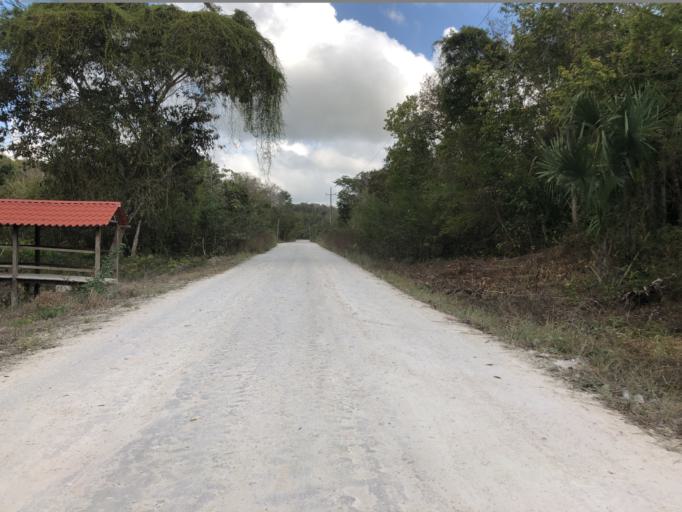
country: MX
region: Quintana Roo
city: Nicolas Bravo
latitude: 18.4574
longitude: -89.3056
